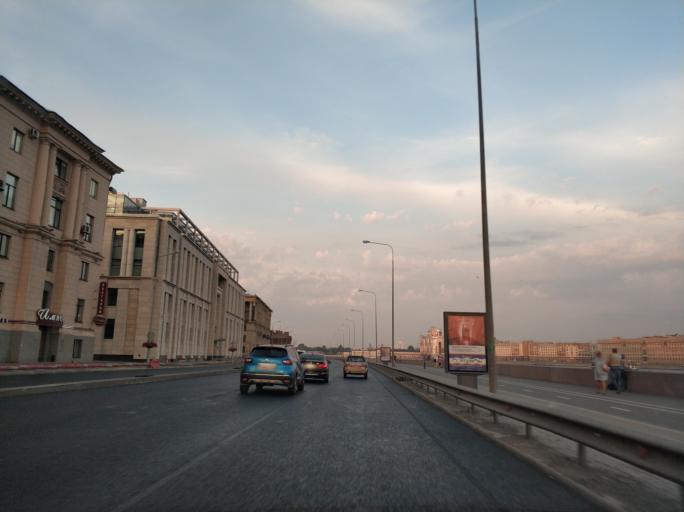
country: RU
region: Leningrad
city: Finlyandskiy
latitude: 59.9530
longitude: 30.3574
